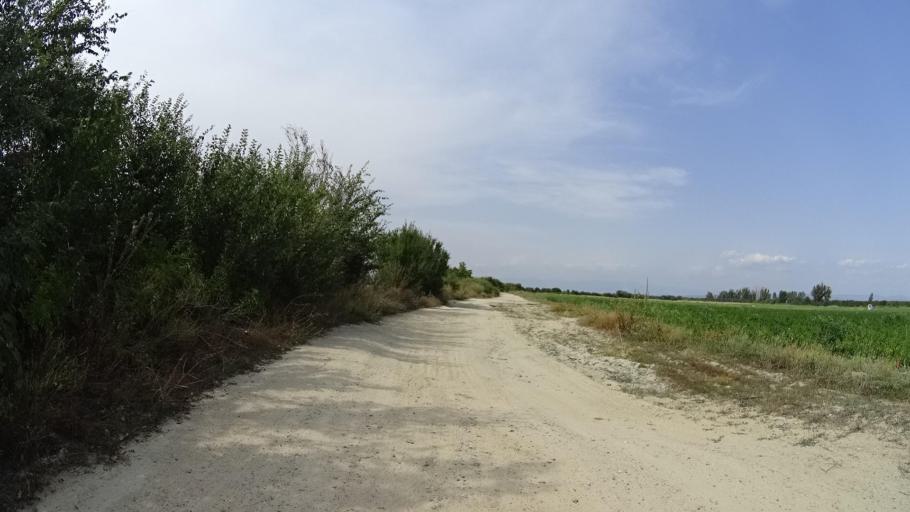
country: BG
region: Plovdiv
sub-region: Obshtina Kaloyanovo
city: Kaloyanovo
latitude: 42.2930
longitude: 24.7960
